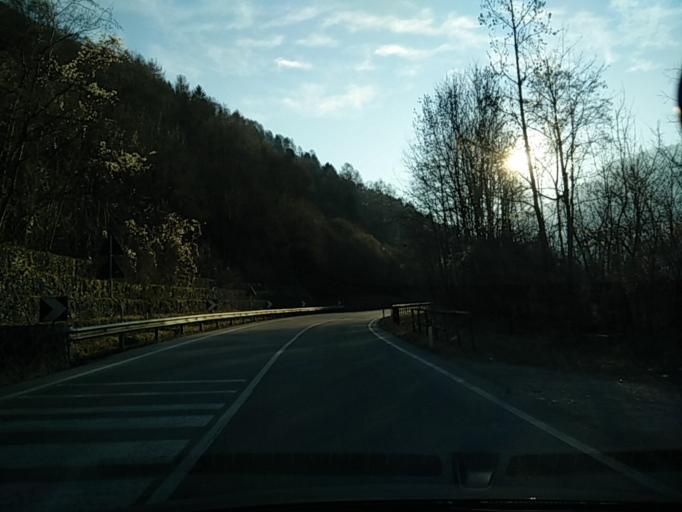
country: IT
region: Veneto
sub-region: Provincia di Belluno
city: Farra d'Alpago
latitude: 46.1056
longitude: 12.3538
